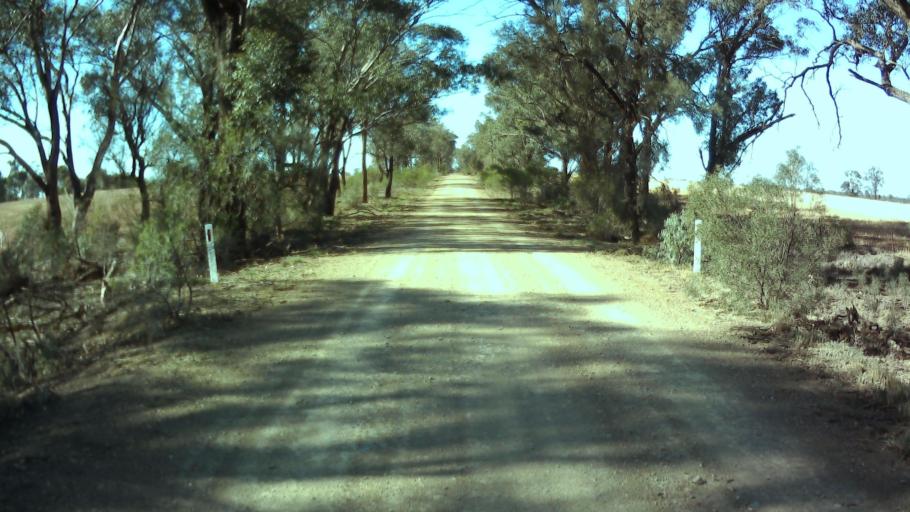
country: AU
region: New South Wales
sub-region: Weddin
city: Grenfell
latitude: -33.9050
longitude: 147.8778
